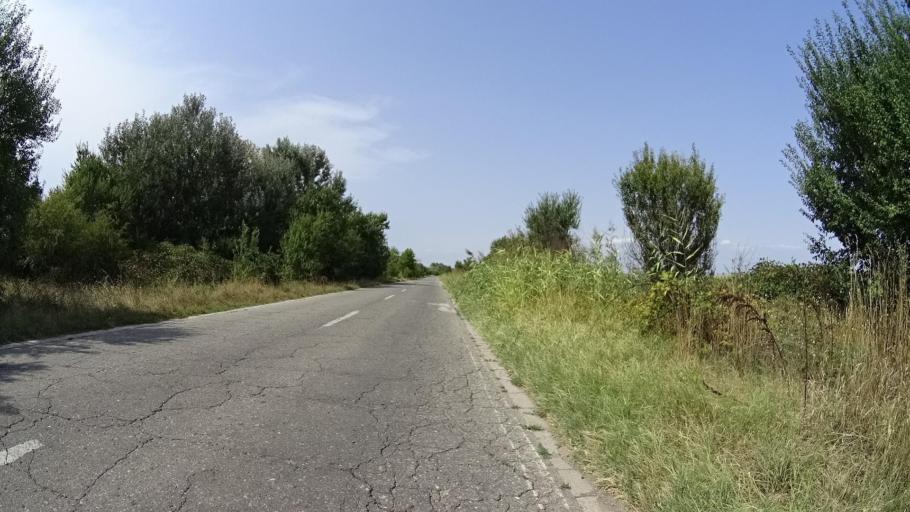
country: BG
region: Plovdiv
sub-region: Obshtina Plovdiv
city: Plovdiv
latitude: 42.2283
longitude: 24.7861
